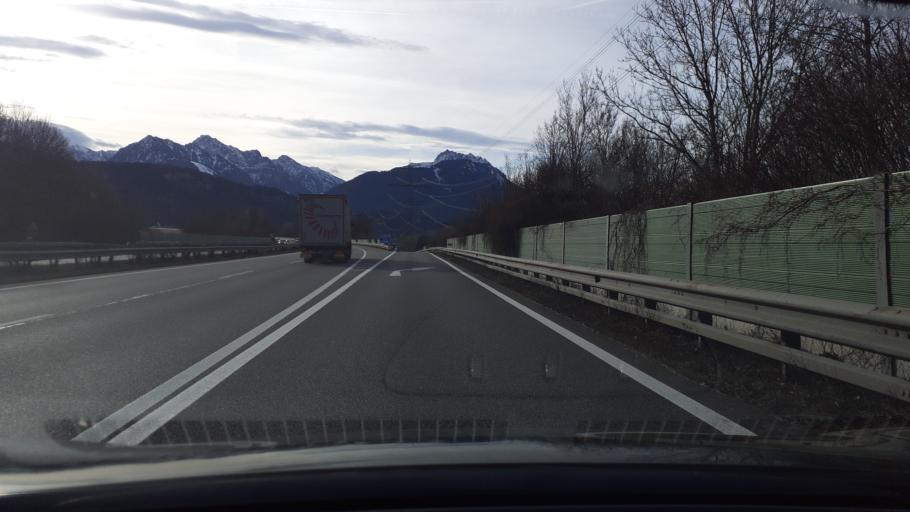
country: AT
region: Vorarlberg
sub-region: Politischer Bezirk Feldkirch
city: Rankweil
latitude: 47.2789
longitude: 9.6225
